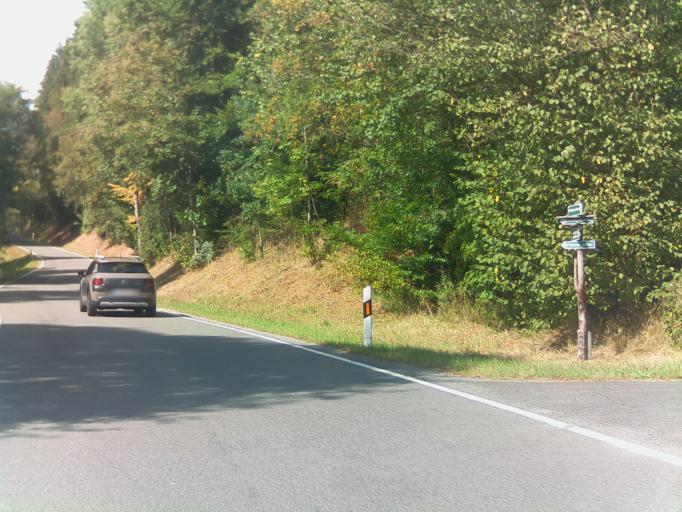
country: DE
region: Thuringia
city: Schwarza
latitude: 50.6498
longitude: 10.5177
